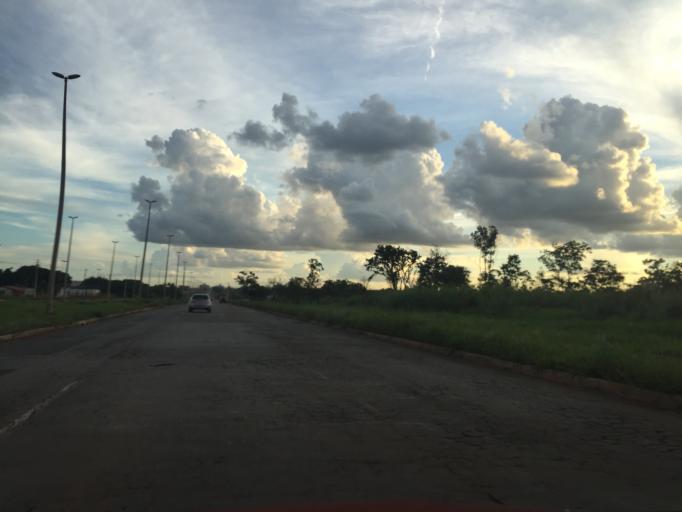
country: BR
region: Federal District
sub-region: Brasilia
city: Brasilia
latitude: -15.7969
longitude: -47.9910
